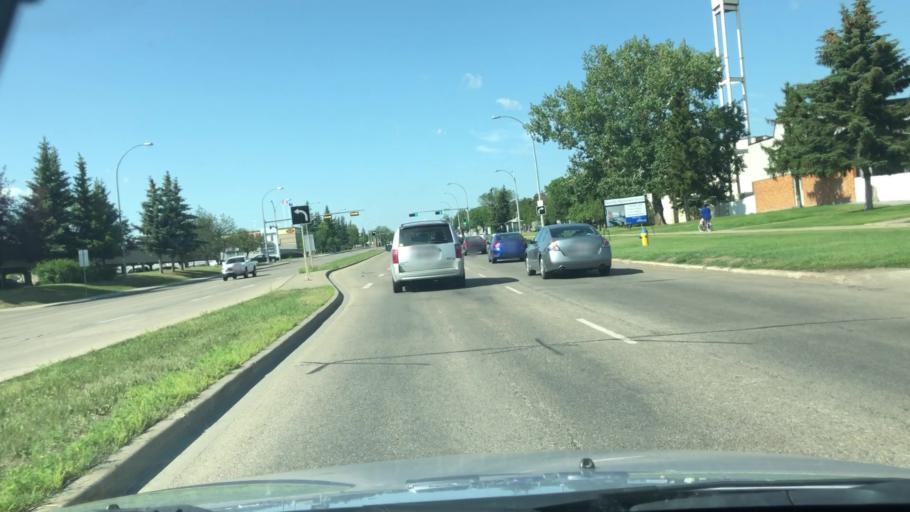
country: CA
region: Alberta
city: Edmonton
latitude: 53.6006
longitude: -113.4429
